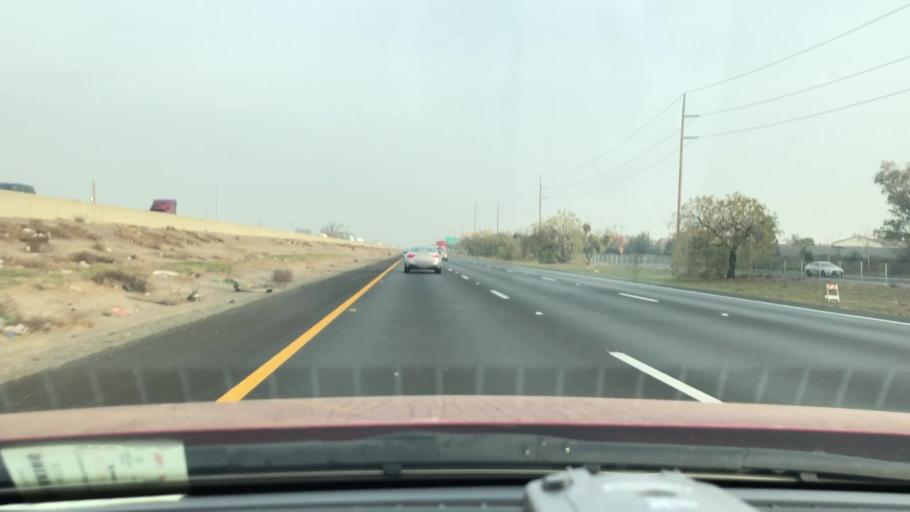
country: US
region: California
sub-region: San Joaquin County
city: Lathrop
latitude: 37.8365
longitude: -121.2865
